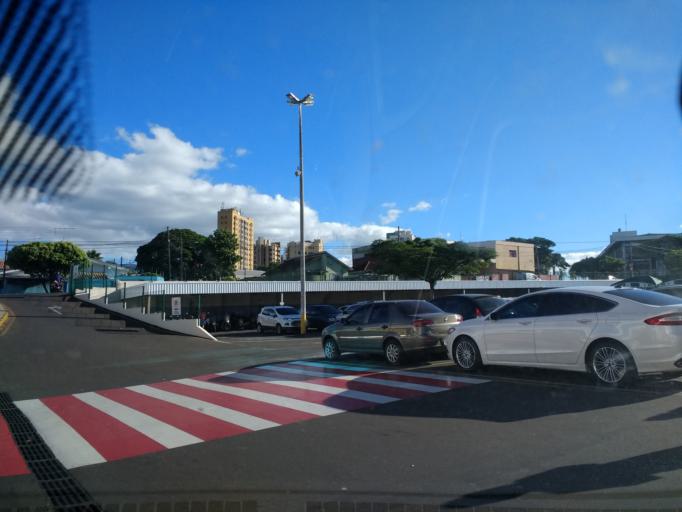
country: BR
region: Parana
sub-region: Londrina
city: Londrina
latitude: -23.3307
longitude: -51.1510
